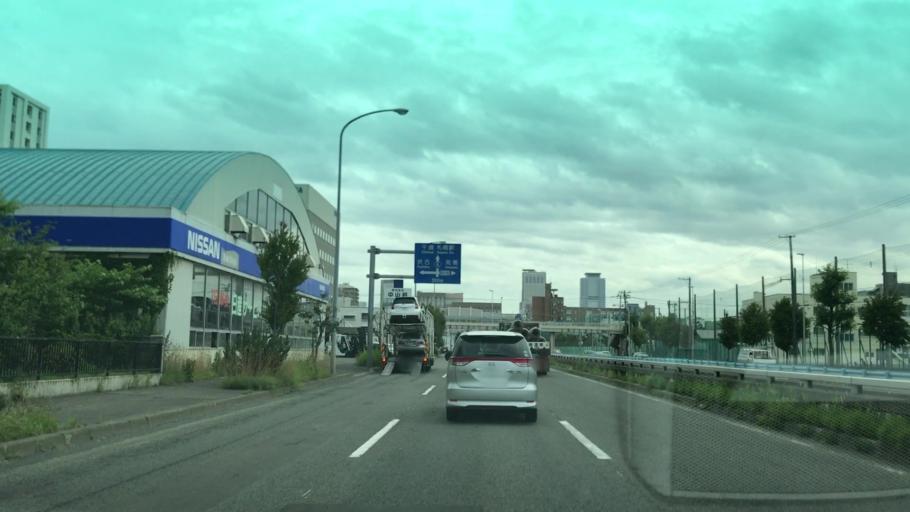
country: JP
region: Hokkaido
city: Sapporo
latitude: 43.0851
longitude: 141.3493
